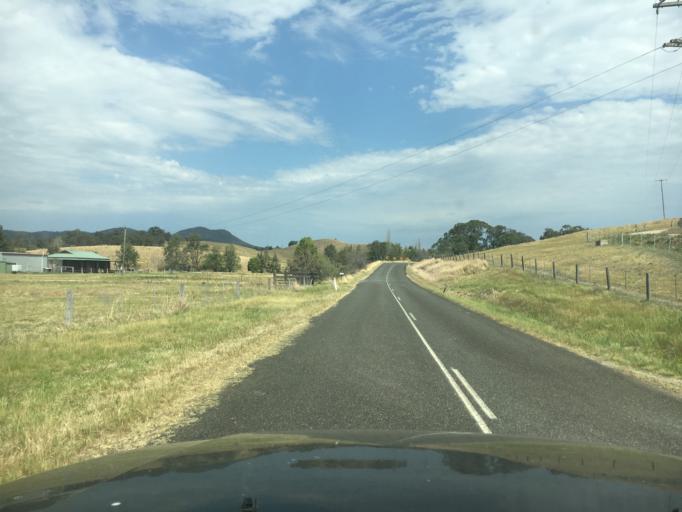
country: AU
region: New South Wales
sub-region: Cessnock
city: Branxton
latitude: -32.4998
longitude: 151.3328
